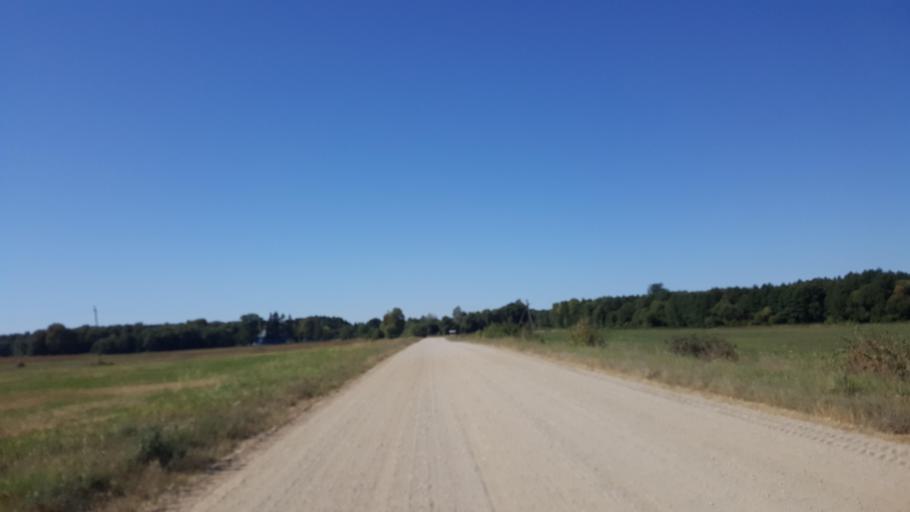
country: BY
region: Brest
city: Charnawchytsy
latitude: 52.3293
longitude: 23.6182
